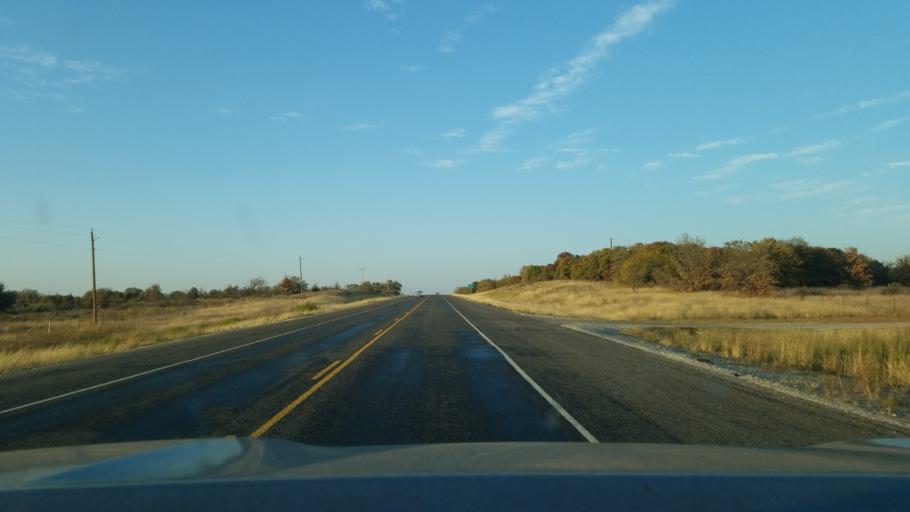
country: US
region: Texas
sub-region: Eastland County
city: Cisco
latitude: 32.3165
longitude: -98.9576
